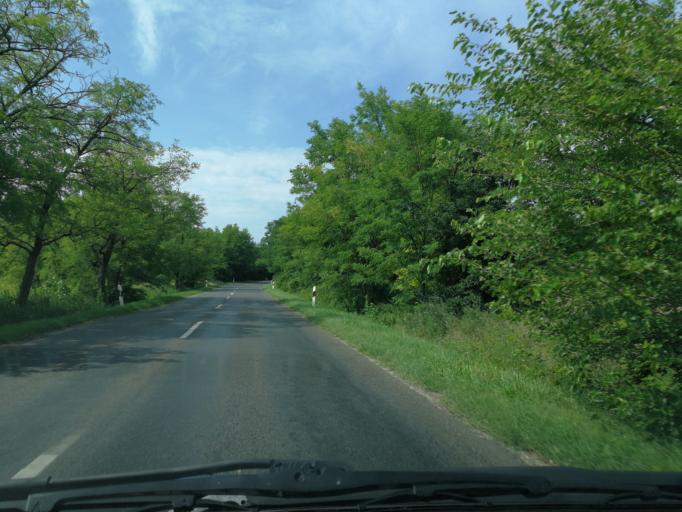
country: HU
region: Bacs-Kiskun
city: Davod
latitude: 46.0069
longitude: 18.9330
